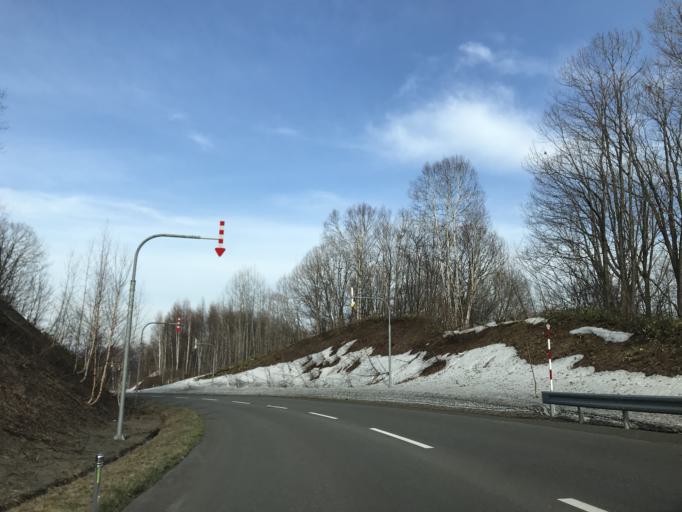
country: JP
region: Hokkaido
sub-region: Asahikawa-shi
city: Asahikawa
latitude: 43.6969
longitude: 142.3267
